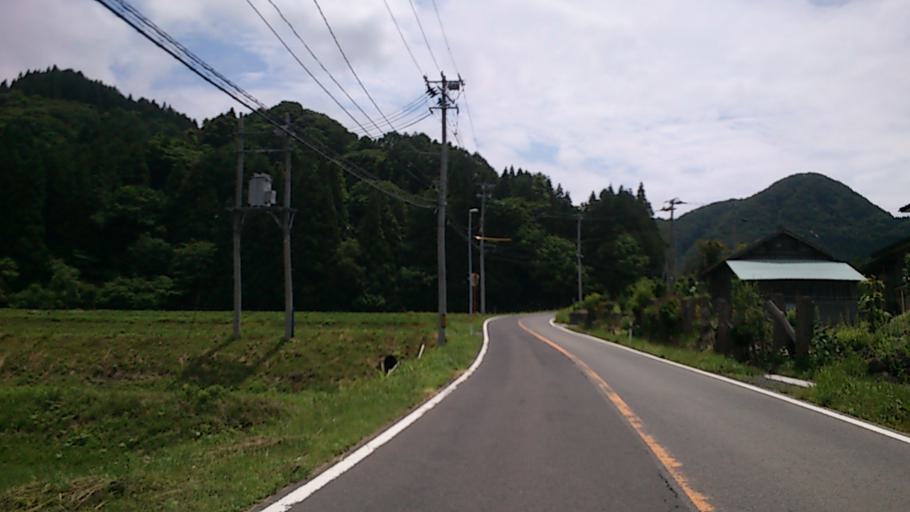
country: JP
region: Yamagata
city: Kaminoyama
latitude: 38.1325
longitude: 140.3621
